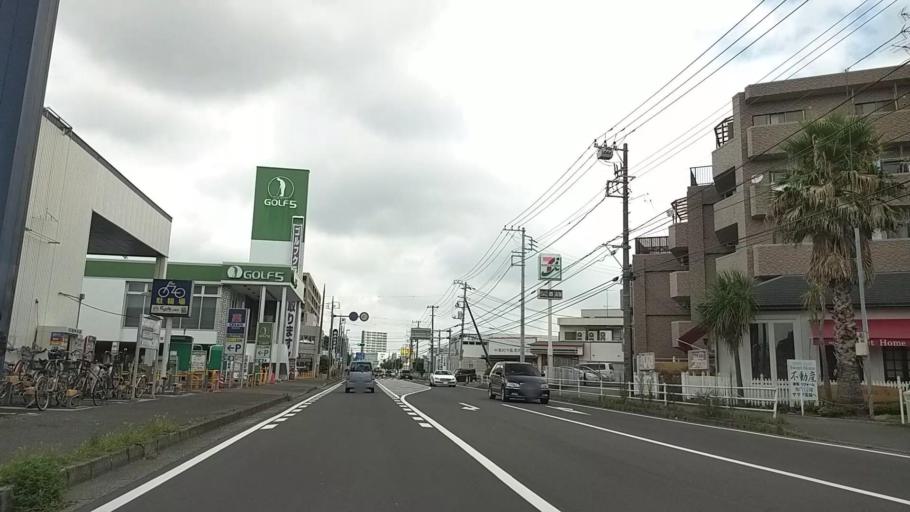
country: JP
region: Kanagawa
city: Minami-rinkan
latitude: 35.5111
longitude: 139.4595
